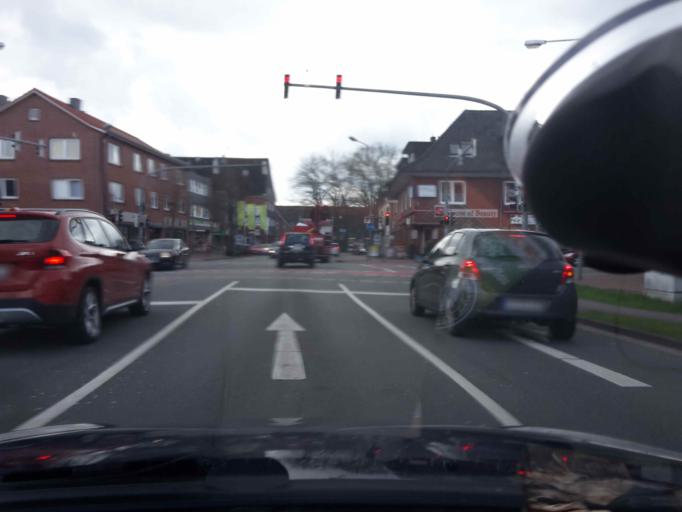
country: DE
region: Lower Saxony
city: Buchholz in der Nordheide
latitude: 53.3313
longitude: 9.8821
